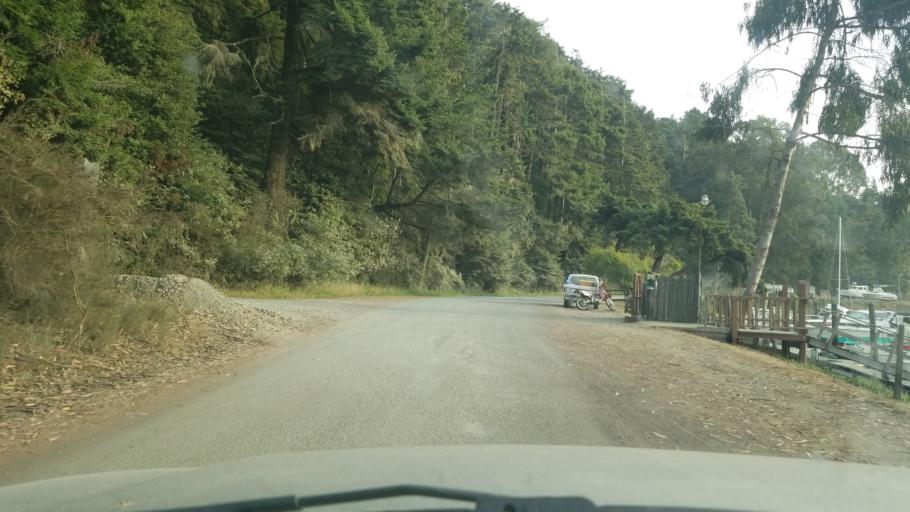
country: US
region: California
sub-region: Mendocino County
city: Fort Bragg
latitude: 39.4310
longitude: -123.7947
